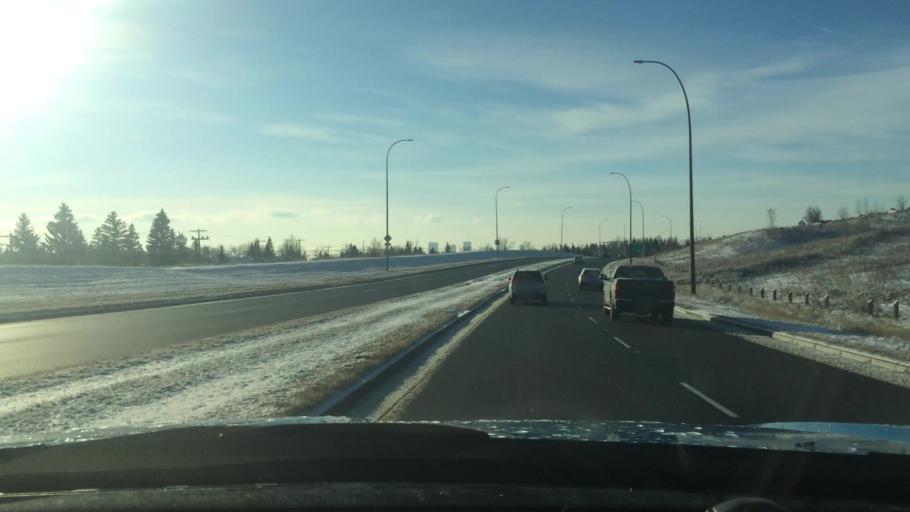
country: CA
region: Alberta
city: Calgary
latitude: 51.1123
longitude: -114.0833
